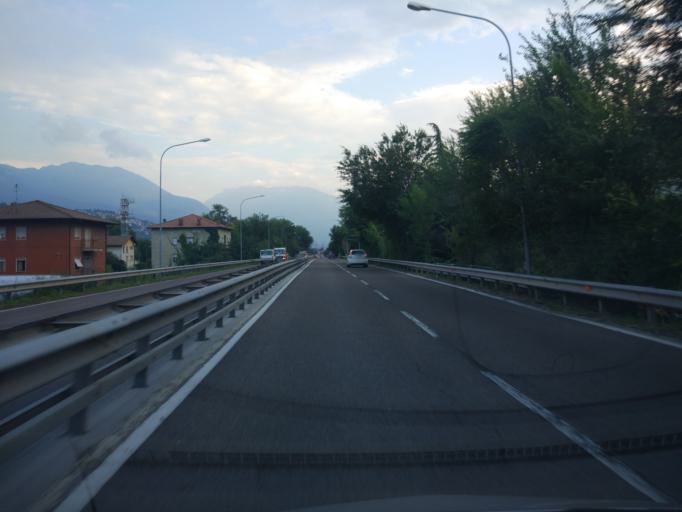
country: IT
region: Trentino-Alto Adige
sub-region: Provincia di Trento
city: Meano
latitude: 46.1078
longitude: 11.1089
